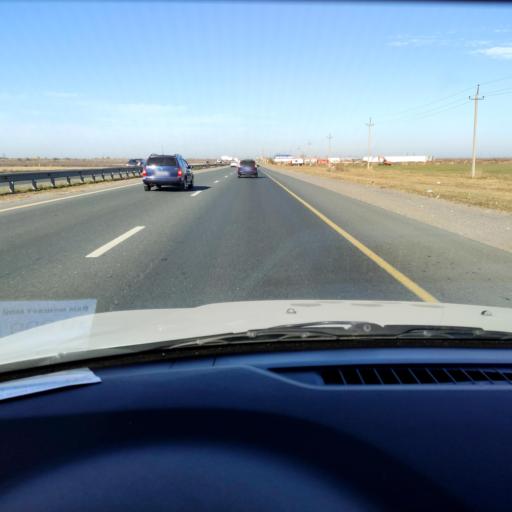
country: RU
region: Samara
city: Zhigulevsk
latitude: 53.5500
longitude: 49.5081
